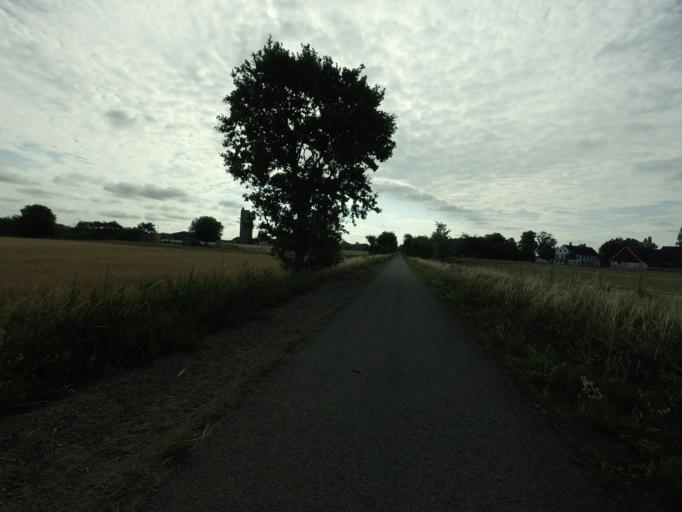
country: SE
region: Skane
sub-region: Helsingborg
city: Odakra
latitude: 56.1784
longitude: 12.6724
